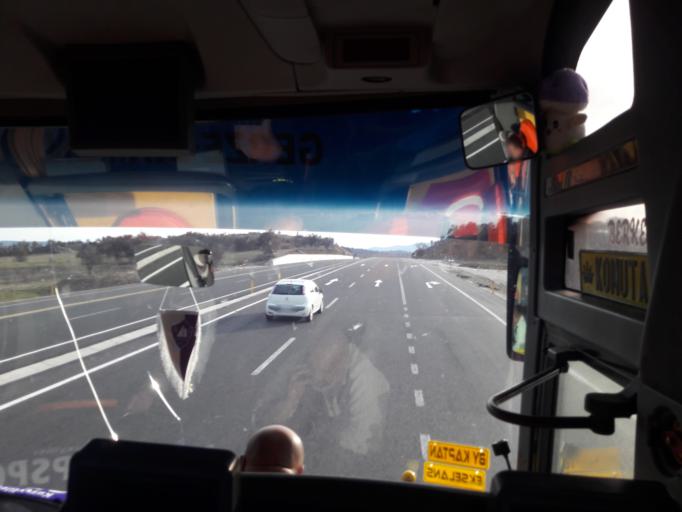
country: TR
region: Cankiri
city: Ilgaz
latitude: 40.8548
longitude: 33.6083
